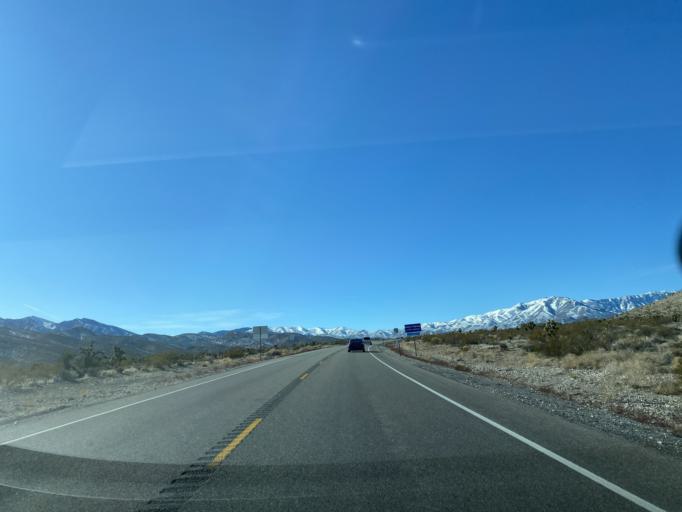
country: US
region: Nevada
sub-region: Clark County
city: Summerlin South
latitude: 36.2837
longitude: -115.4383
